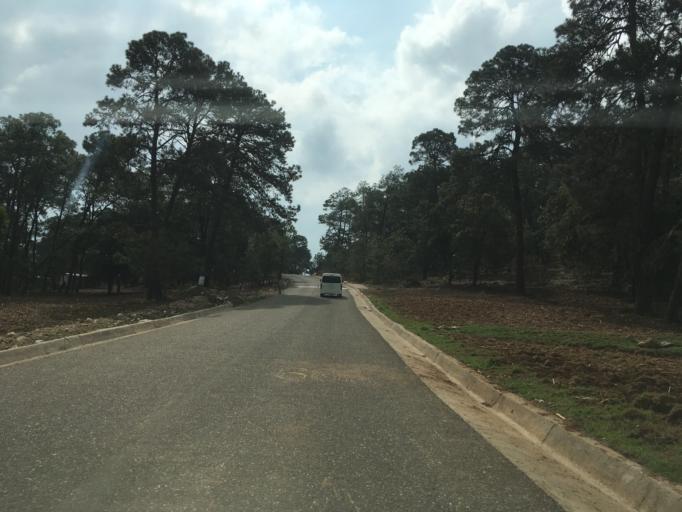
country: MX
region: Oaxaca
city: Santiago Tilantongo
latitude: 17.2133
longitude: -97.2815
